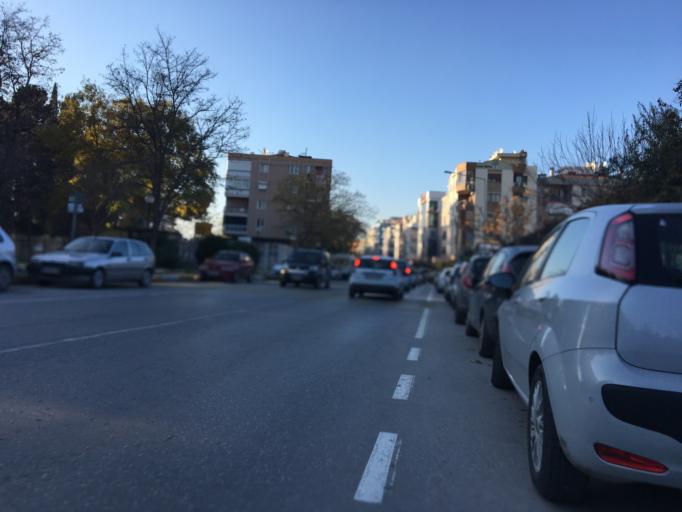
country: TR
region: Izmir
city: Buca
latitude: 38.3866
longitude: 27.1646
